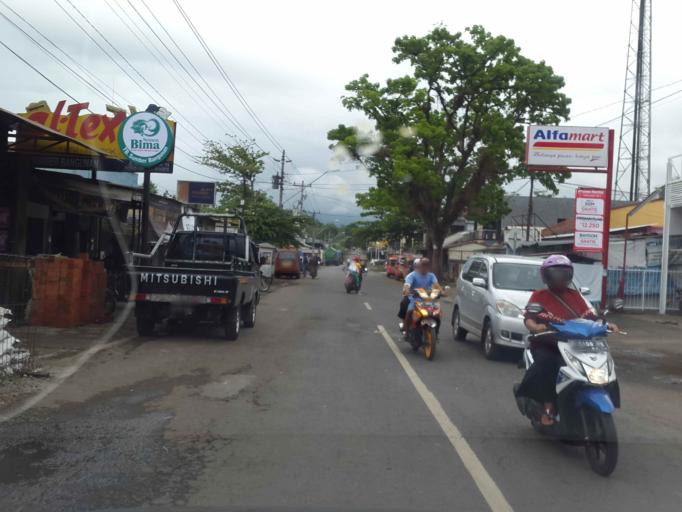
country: ID
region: Central Java
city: Purwokerto
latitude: -7.4201
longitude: 109.2003
